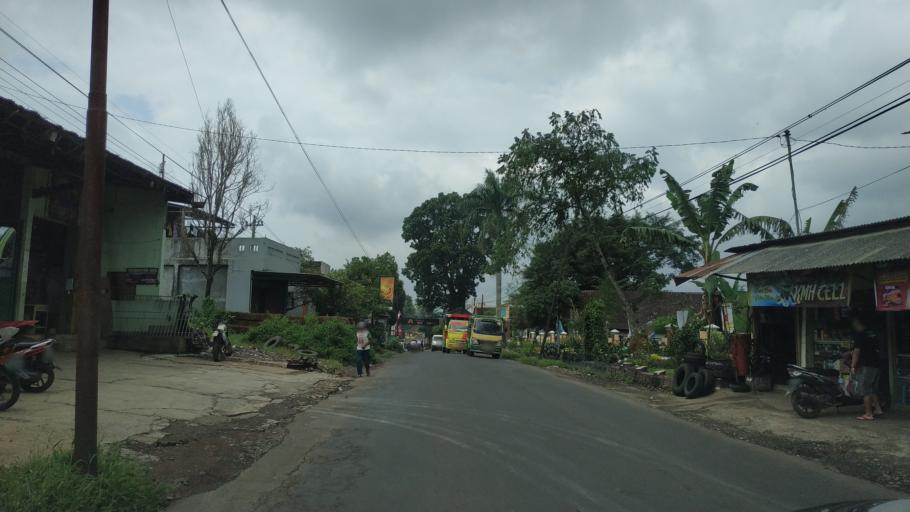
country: ID
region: Central Java
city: Weleri
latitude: -7.0913
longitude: 110.0513
